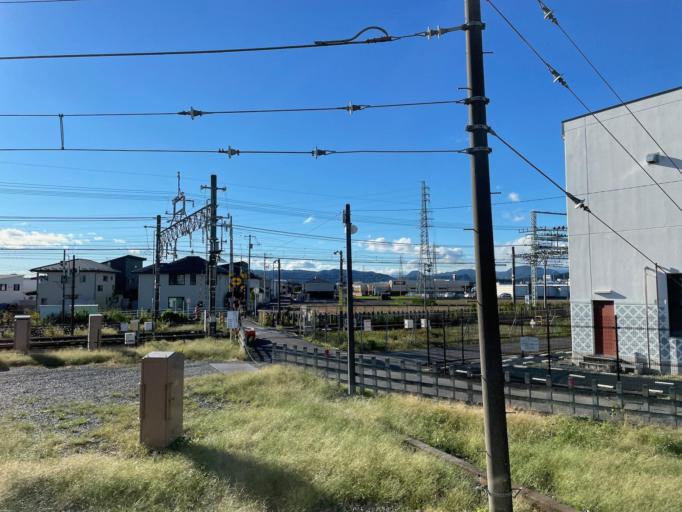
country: JP
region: Tochigi
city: Tochigi
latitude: 36.3958
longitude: 139.7411
